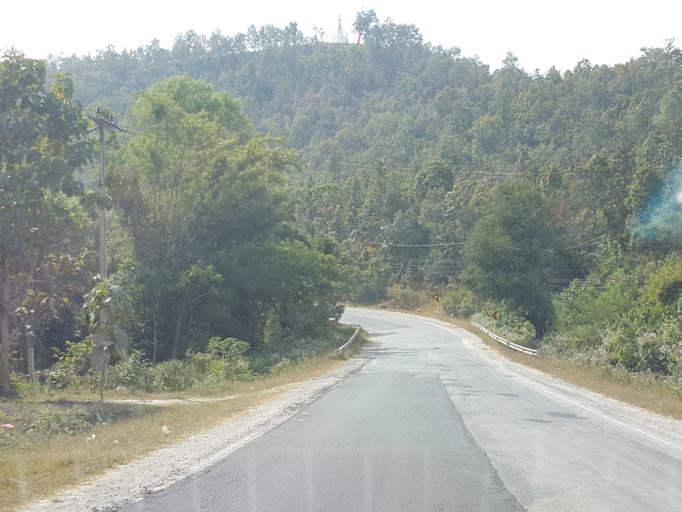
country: TH
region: Chiang Mai
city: Om Koi
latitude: 17.8108
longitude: 98.3643
